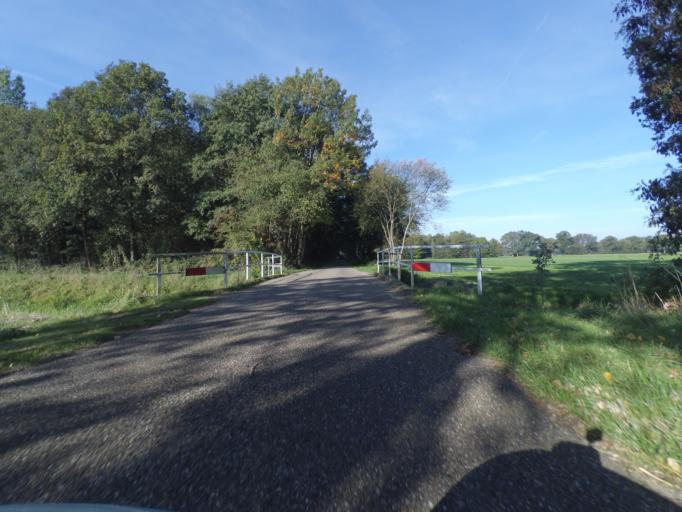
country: NL
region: Gelderland
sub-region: Berkelland
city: Borculo
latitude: 52.0861
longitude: 6.4891
